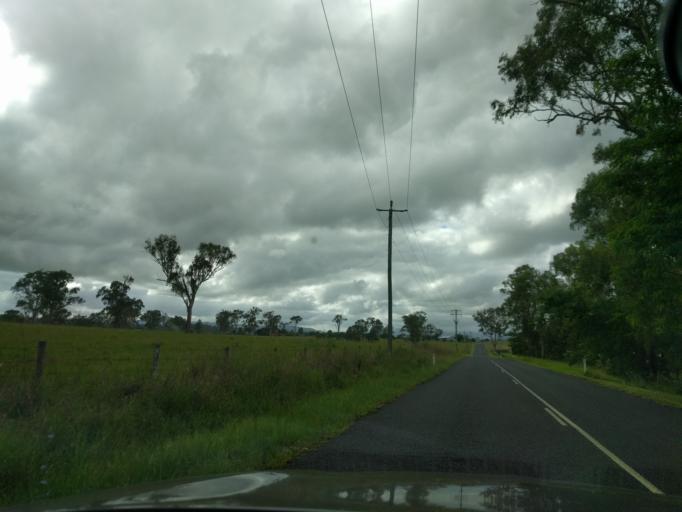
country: AU
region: Queensland
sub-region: Logan
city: Cedar Vale
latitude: -28.0039
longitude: 152.9904
